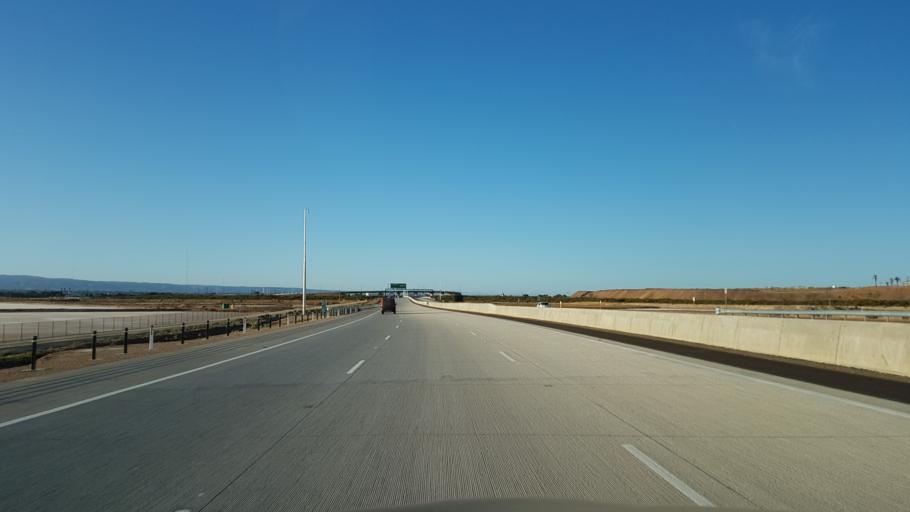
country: AU
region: South Australia
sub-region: Port Adelaide Enfield
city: Enfield
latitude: -34.8182
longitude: 138.5618
